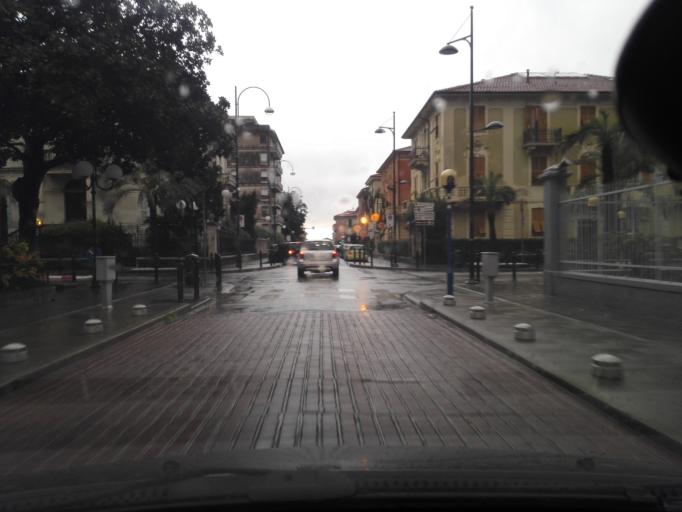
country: IT
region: Liguria
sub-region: Provincia di Genova
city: Chiavari
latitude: 44.3187
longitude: 9.3188
